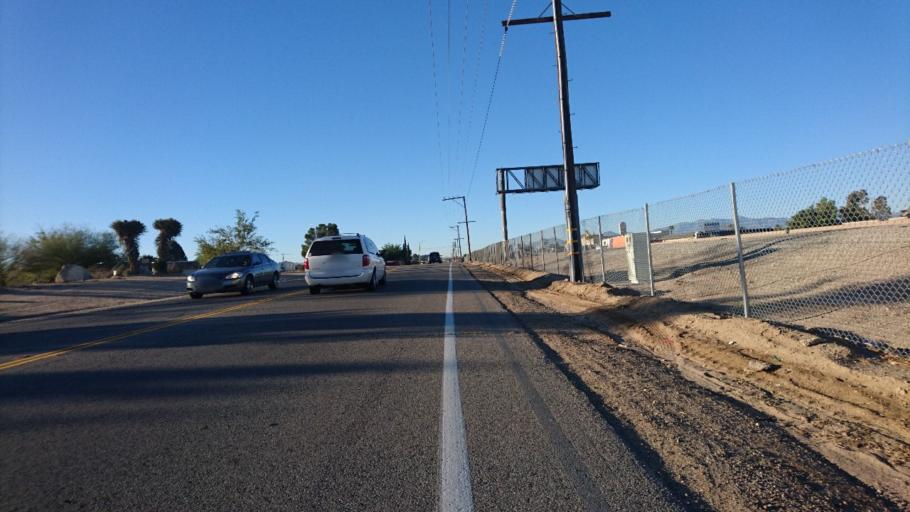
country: US
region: California
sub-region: San Bernardino County
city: Mountain View Acres
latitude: 34.5030
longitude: -117.3240
